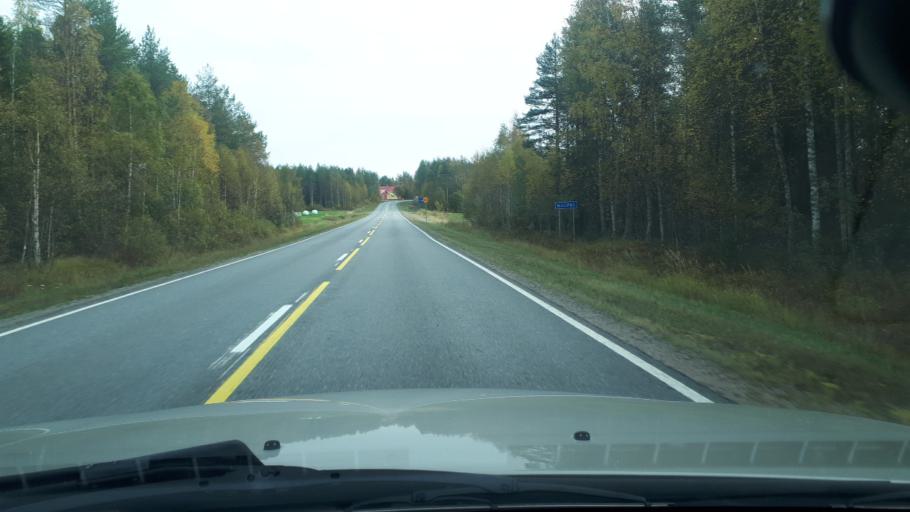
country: FI
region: Lapland
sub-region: Rovaniemi
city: Ranua
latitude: 66.0117
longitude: 26.3067
